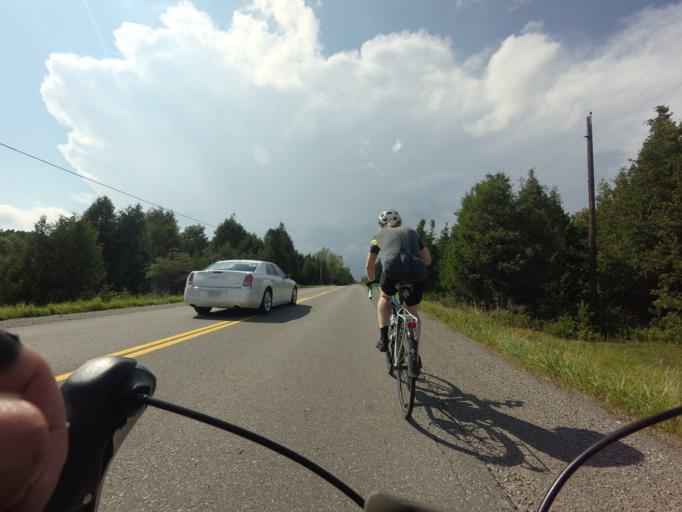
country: CA
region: Ontario
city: Brockville
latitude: 44.7831
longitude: -75.7619
